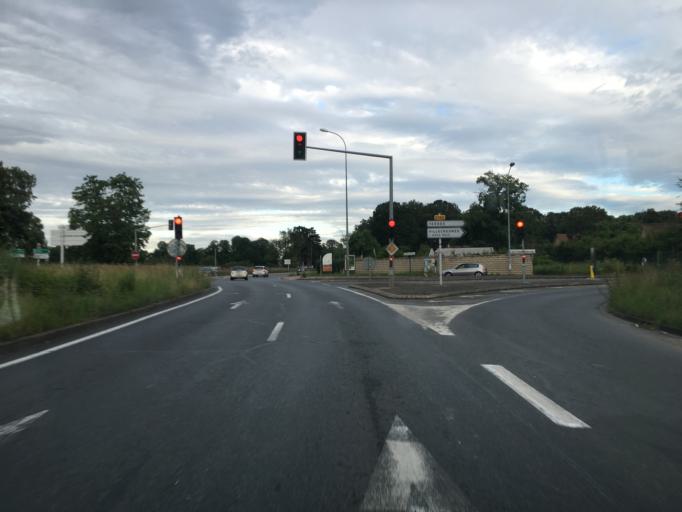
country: FR
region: Ile-de-France
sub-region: Departement du Val-de-Marne
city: Boissy-Saint-Leger
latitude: 48.7347
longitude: 2.5198
